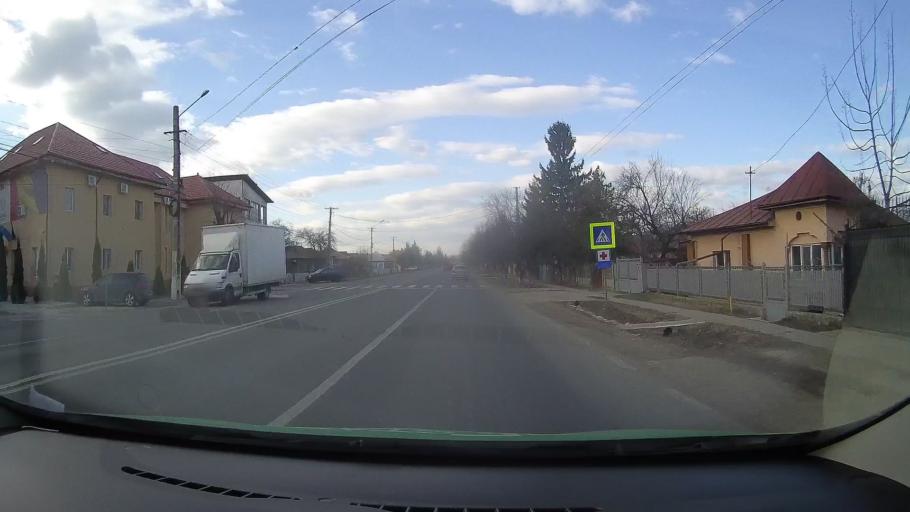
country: RO
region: Dambovita
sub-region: Comuna Ulmi
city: Ulmi
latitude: 44.8956
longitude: 25.5011
